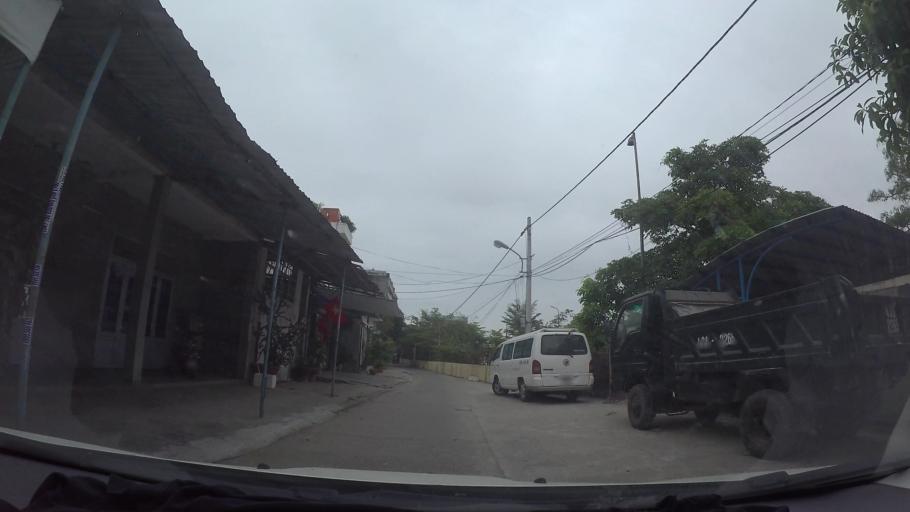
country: VN
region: Da Nang
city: Lien Chieu
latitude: 16.0658
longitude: 108.1527
